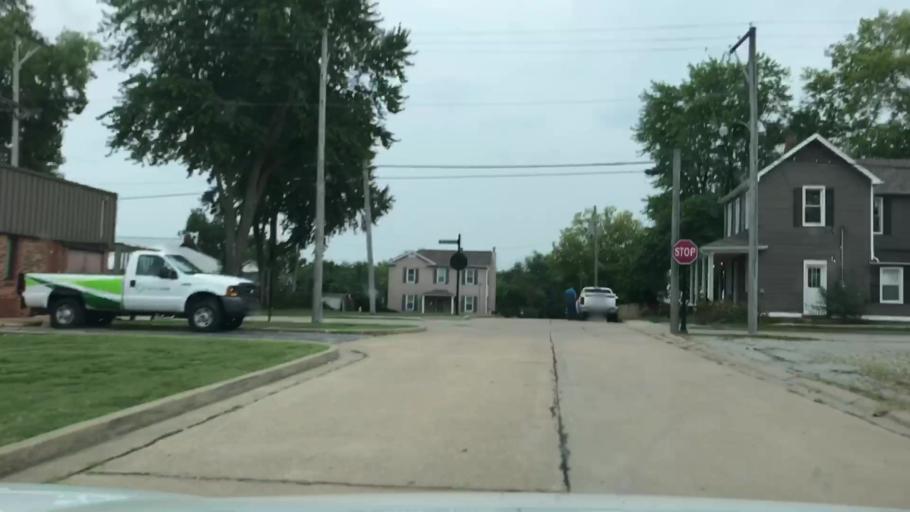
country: US
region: Missouri
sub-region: Saint Charles County
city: Wentzville
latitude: 38.8110
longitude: -90.8520
